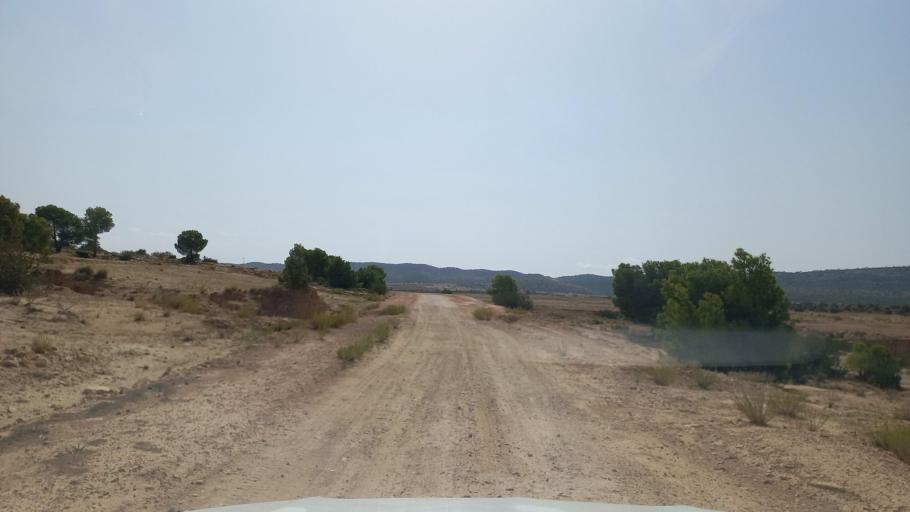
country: TN
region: Al Qasrayn
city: Sbiba
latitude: 35.3954
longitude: 8.9507
